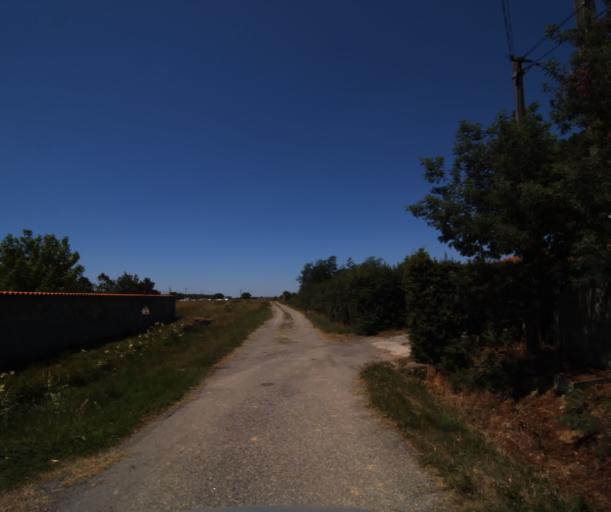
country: FR
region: Midi-Pyrenees
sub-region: Departement de la Haute-Garonne
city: Seysses
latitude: 43.4673
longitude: 1.2995
